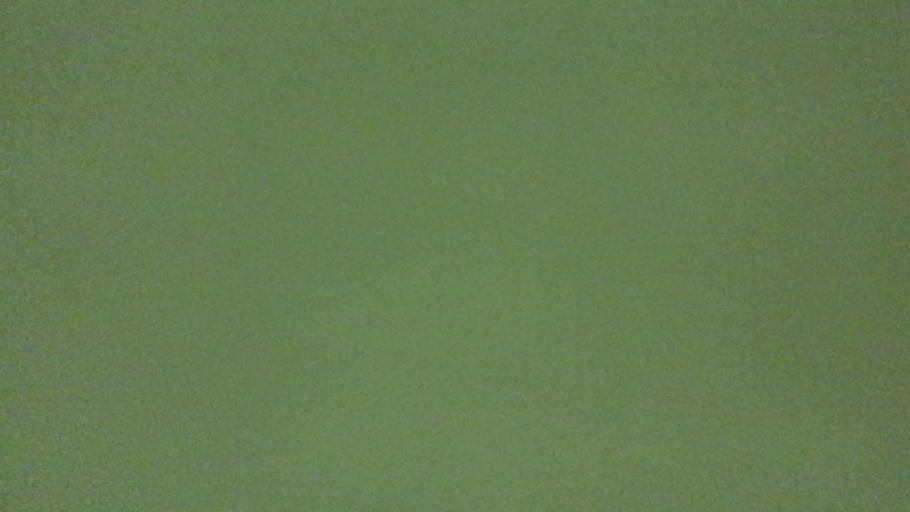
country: JP
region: Hokkaido
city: Sapporo
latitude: 43.1020
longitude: 141.2715
